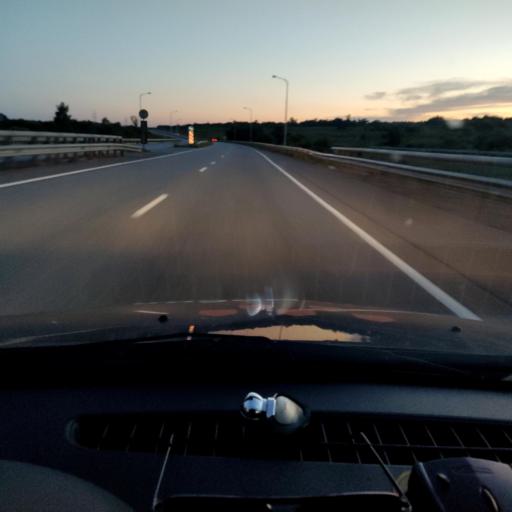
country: RU
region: Belgorod
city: Bekhteyevka
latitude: 50.7549
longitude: 37.0255
